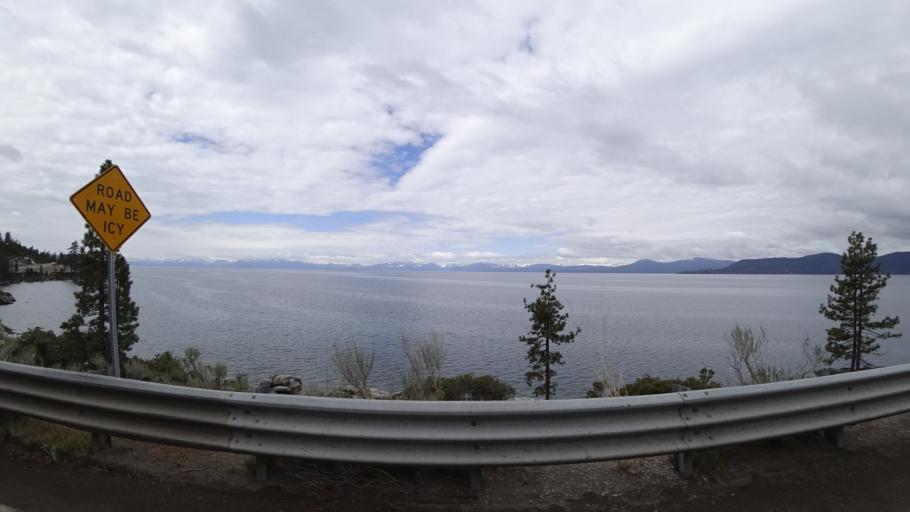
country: US
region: Nevada
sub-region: Washoe County
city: Incline Village
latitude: 39.2147
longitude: -119.9287
